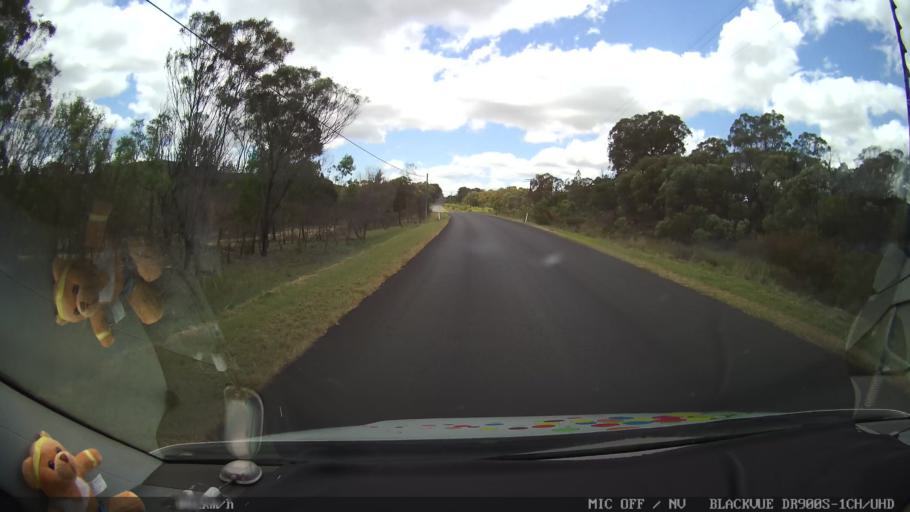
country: AU
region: New South Wales
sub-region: Glen Innes Severn
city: Glen Innes
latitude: -29.4419
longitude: 151.6124
